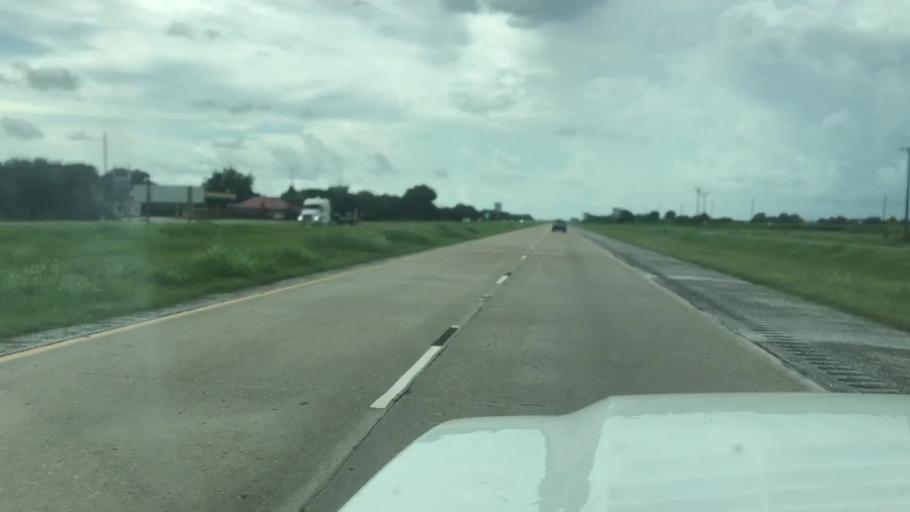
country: US
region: Louisiana
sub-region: Iberia Parish
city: Jeanerette
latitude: 29.8723
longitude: -91.6448
